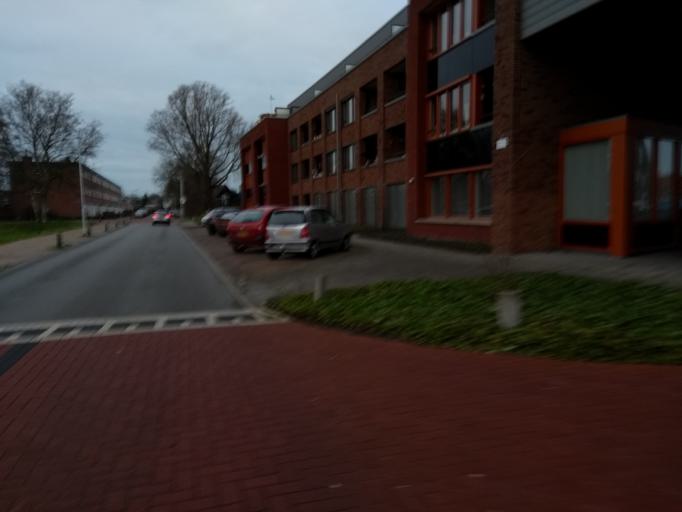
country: NL
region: Friesland
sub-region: Sudwest Fryslan
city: Sneek
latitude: 53.0271
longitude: 5.6547
